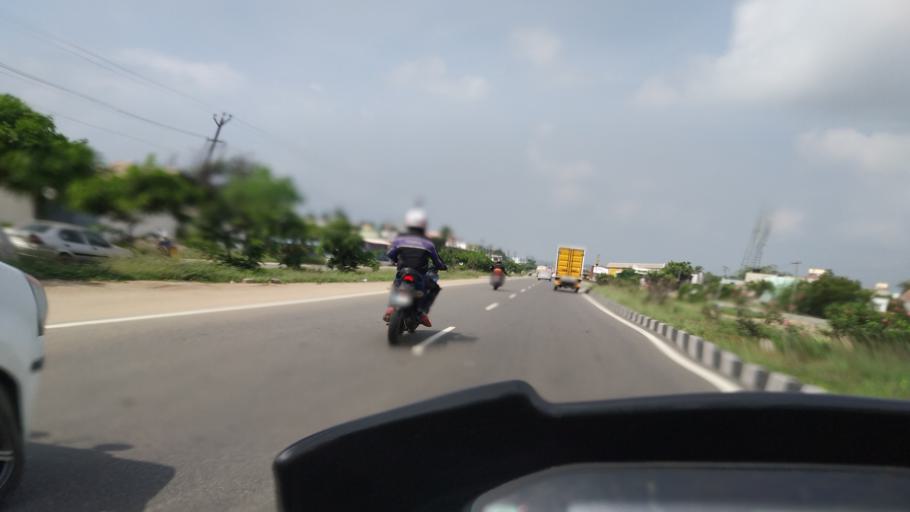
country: IN
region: Tamil Nadu
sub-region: Erode
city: Bhavani
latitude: 11.4336
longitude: 77.6972
